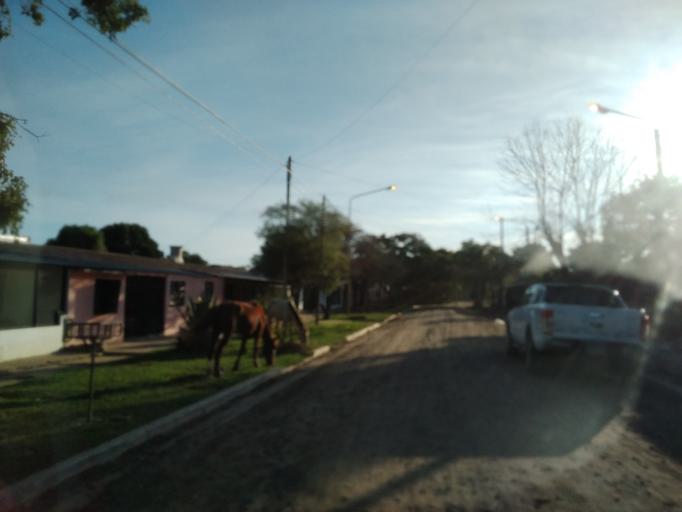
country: AR
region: Corrientes
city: Corrientes
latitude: -27.5012
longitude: -58.8349
